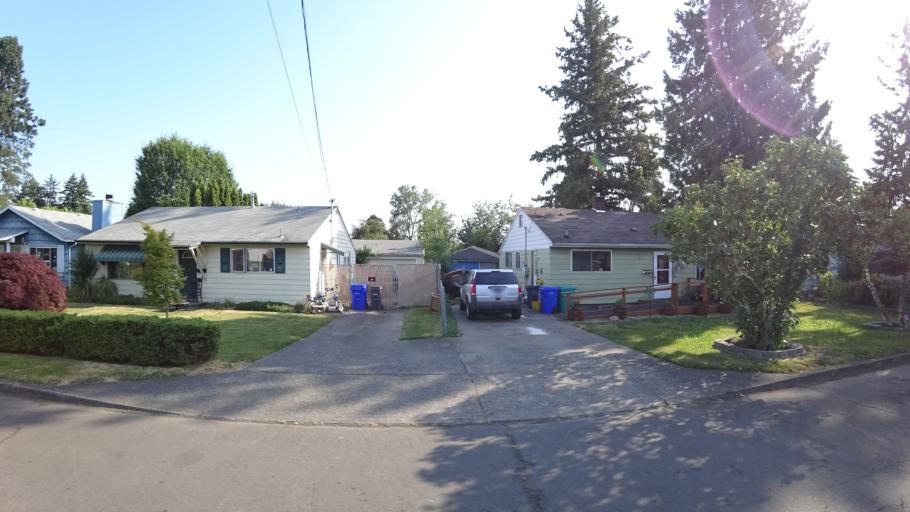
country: US
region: Oregon
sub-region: Washington County
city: West Haven
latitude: 45.5893
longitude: -122.7362
